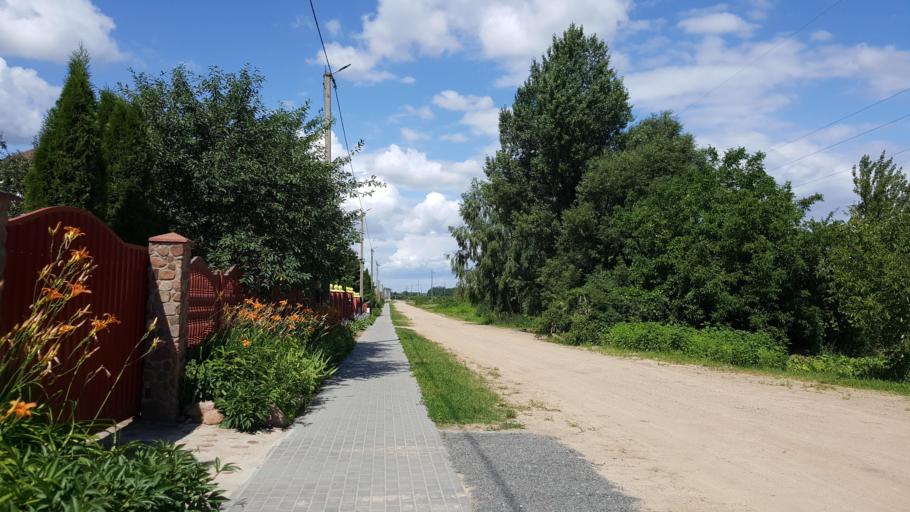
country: BY
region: Brest
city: Kamyanyets
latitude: 52.3926
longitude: 23.8183
